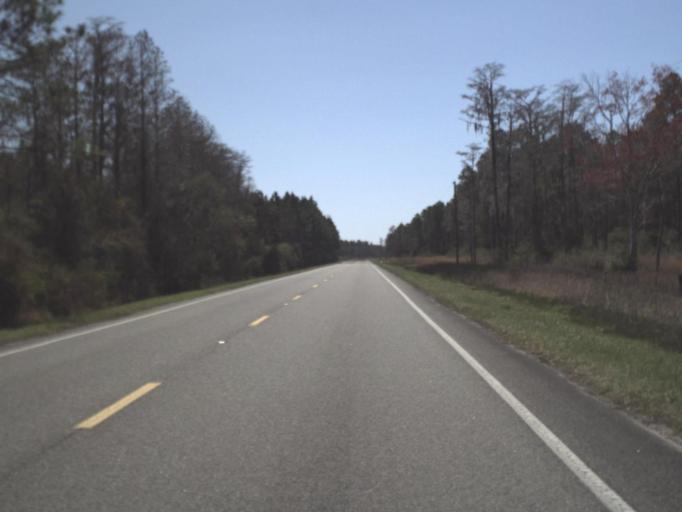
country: US
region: Florida
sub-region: Leon County
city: Woodville
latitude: 30.2764
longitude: -84.0424
